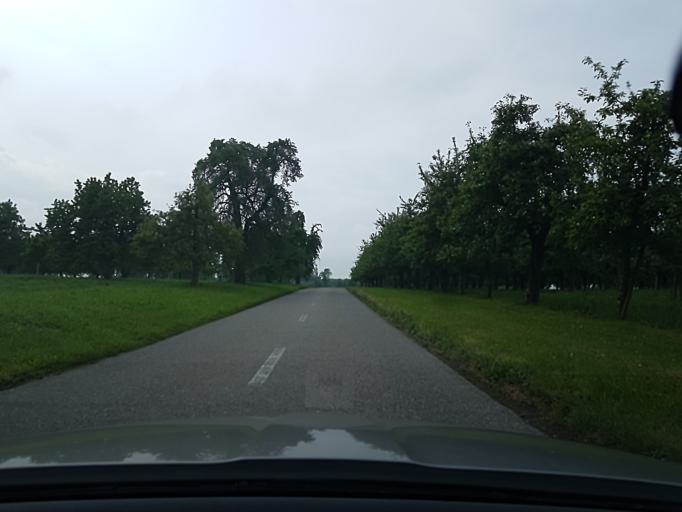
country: CH
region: Thurgau
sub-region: Arbon District
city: Roggwil
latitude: 47.5025
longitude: 9.3935
